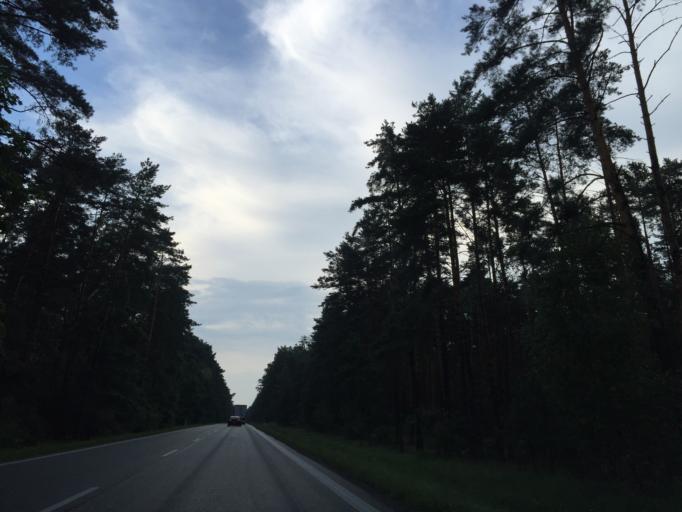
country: PL
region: Masovian Voivodeship
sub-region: Powiat ostrowski
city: Brok
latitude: 52.7110
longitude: 21.8482
